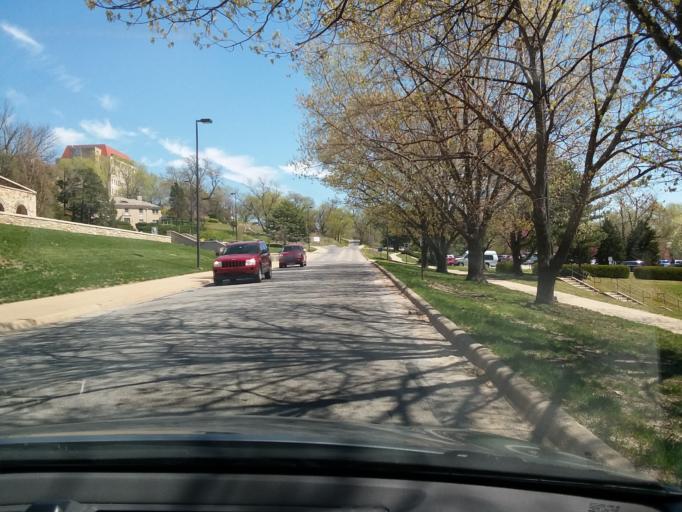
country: US
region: Kansas
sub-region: Douglas County
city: Lawrence
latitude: 38.9552
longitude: -95.2461
